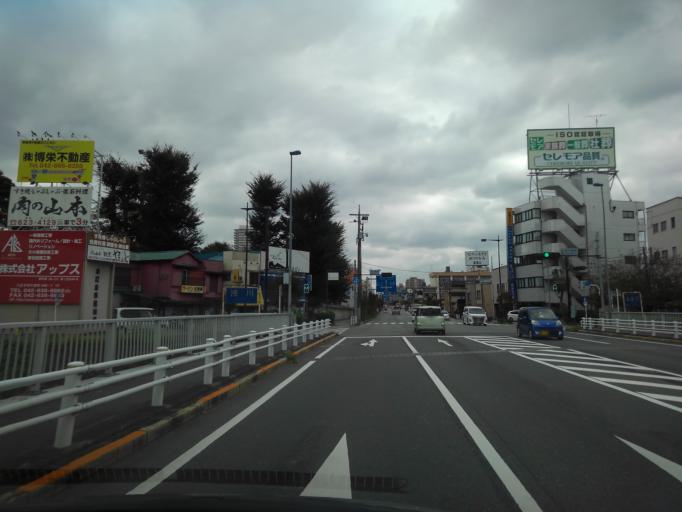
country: JP
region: Tokyo
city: Hachioji
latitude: 35.6662
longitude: 139.3303
